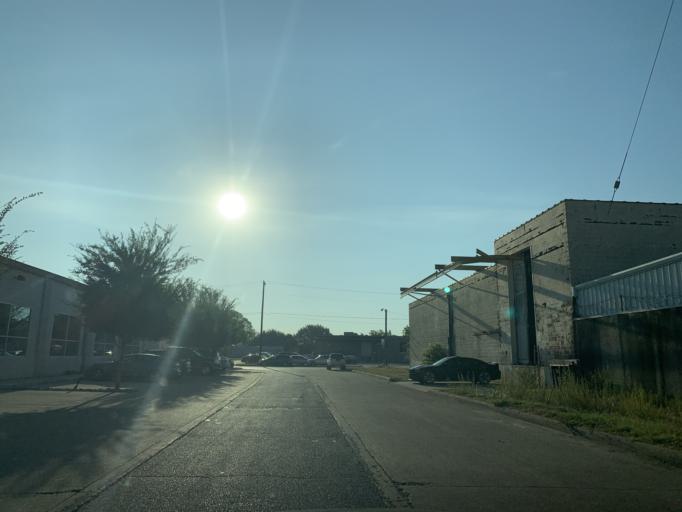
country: US
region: Texas
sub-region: Tarrant County
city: Fort Worth
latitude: 32.7602
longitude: -97.3502
